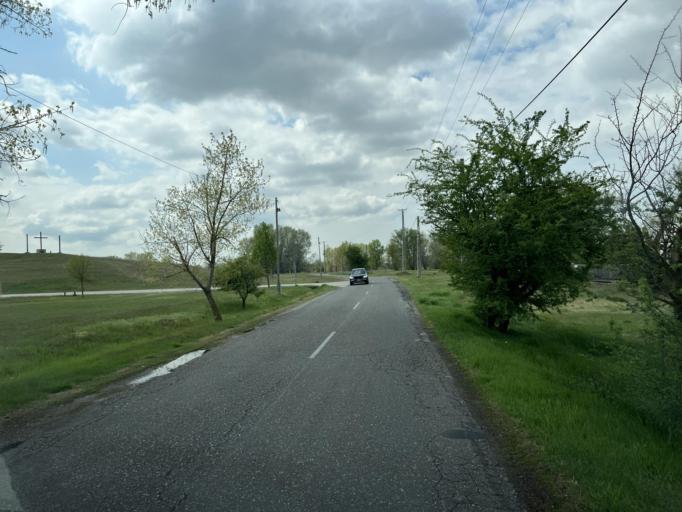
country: HU
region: Pest
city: Orkeny
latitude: 47.0789
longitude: 19.3654
